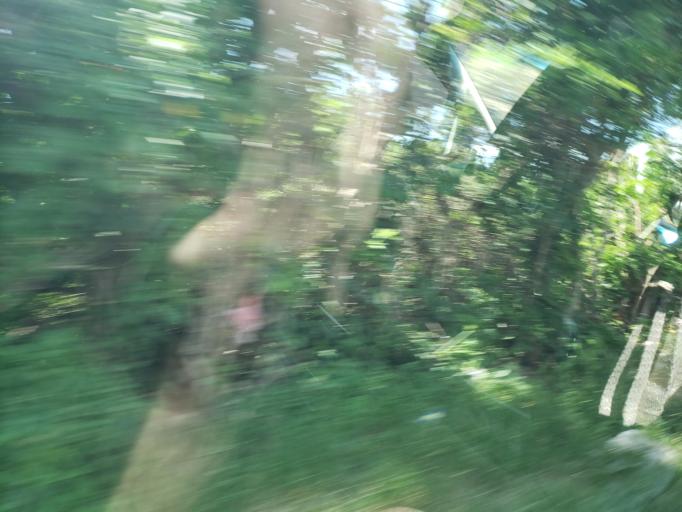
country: ID
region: Bali
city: Kangin
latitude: -8.8305
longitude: 115.1497
